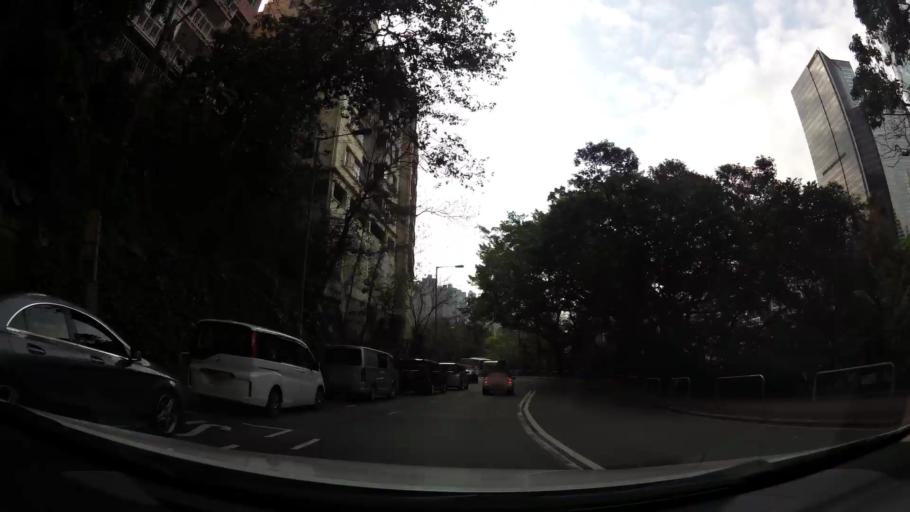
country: HK
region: Central and Western
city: Central
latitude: 22.2759
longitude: 114.1608
